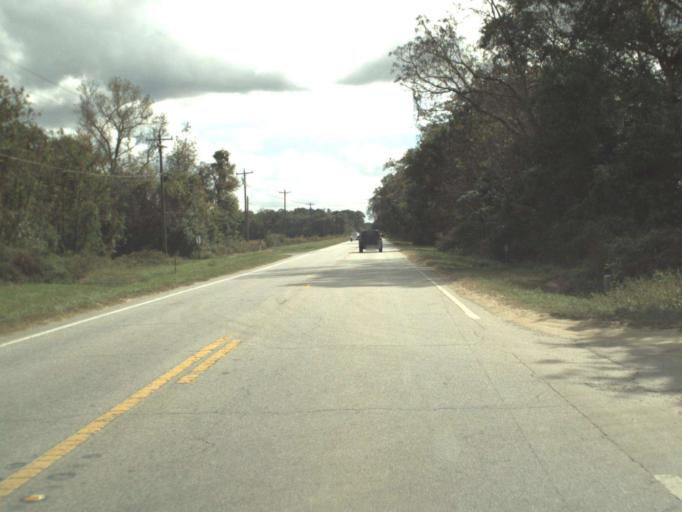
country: US
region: Florida
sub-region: Gadsden County
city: Gretna
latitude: 30.6728
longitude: -84.6158
